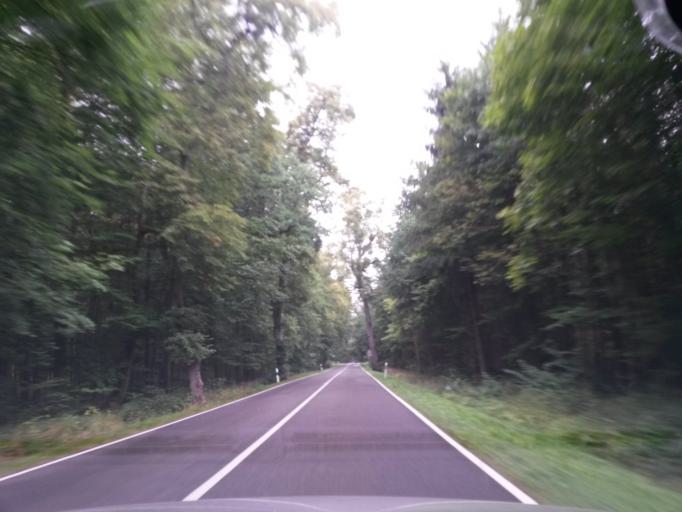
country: DE
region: Brandenburg
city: Gerswalde
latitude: 53.1457
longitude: 13.8591
